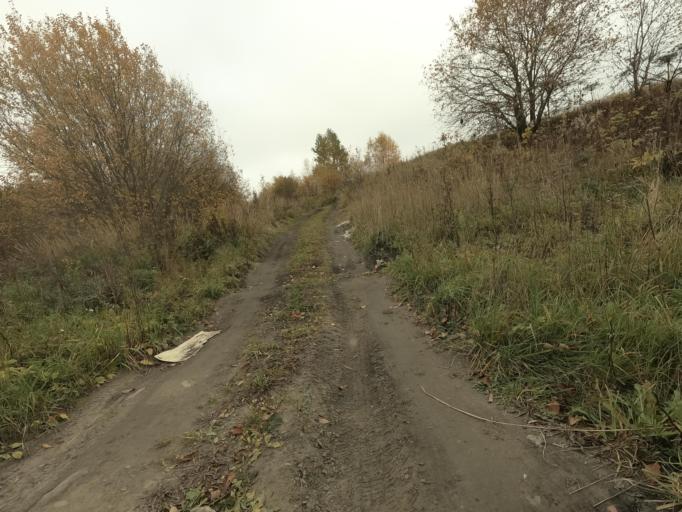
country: RU
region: Leningrad
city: Kirovsk
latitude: 59.8478
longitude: 30.9666
